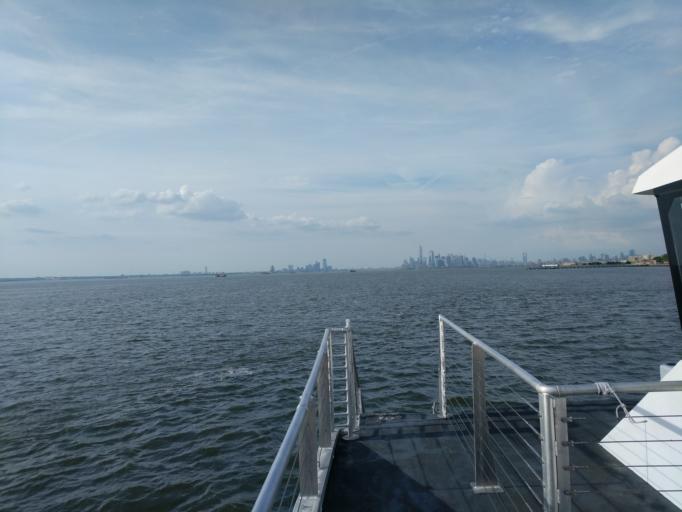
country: US
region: New York
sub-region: Kings County
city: Bensonhurst
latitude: 40.6323
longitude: -74.0435
